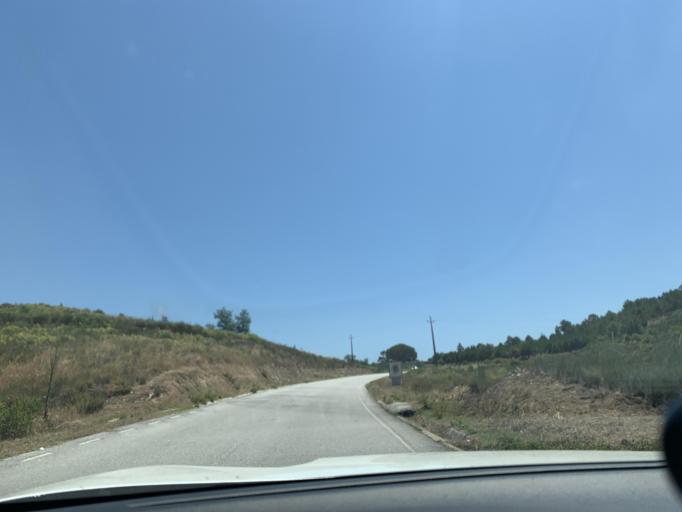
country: PT
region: Viseu
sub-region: Mangualde
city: Mangualde
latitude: 40.5635
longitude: -7.7006
